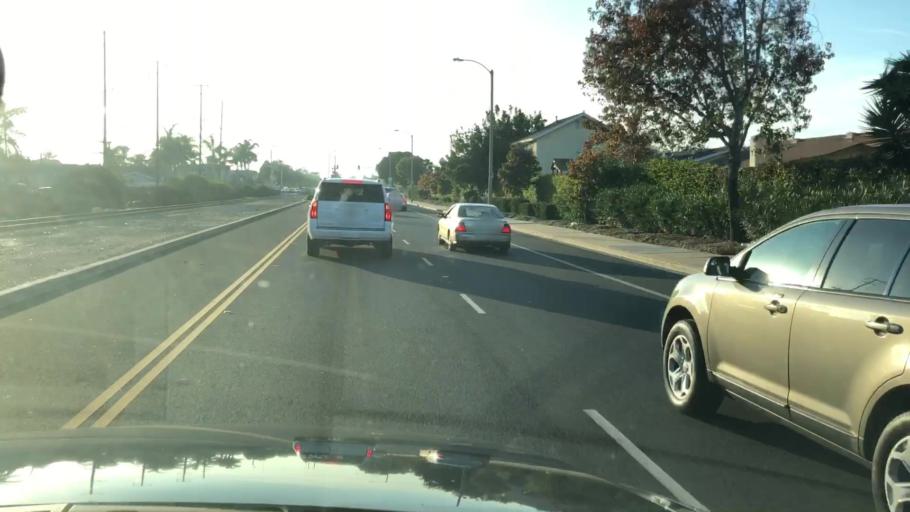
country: US
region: California
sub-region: Ventura County
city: Oxnard
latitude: 34.1903
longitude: -119.1927
